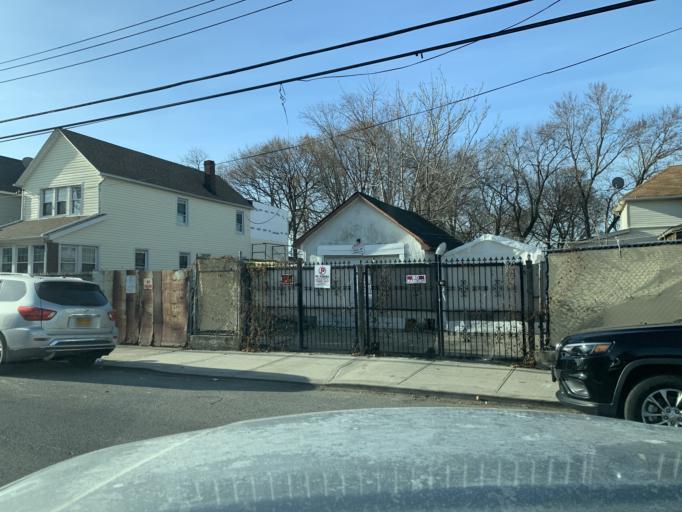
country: US
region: New York
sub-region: Queens County
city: Jamaica
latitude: 40.7024
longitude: -73.7867
